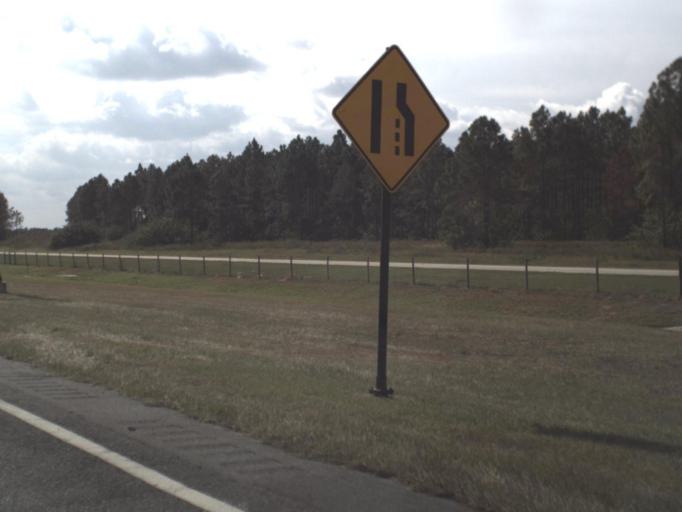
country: US
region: Florida
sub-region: Polk County
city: Auburndale
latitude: 28.1101
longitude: -81.8321
